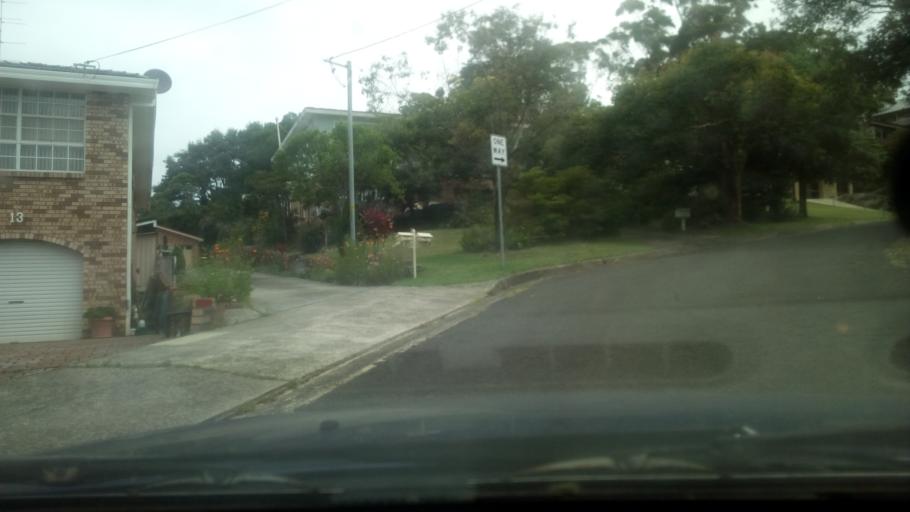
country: AU
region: New South Wales
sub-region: Wollongong
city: Mangerton
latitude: -34.4308
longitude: 150.8802
